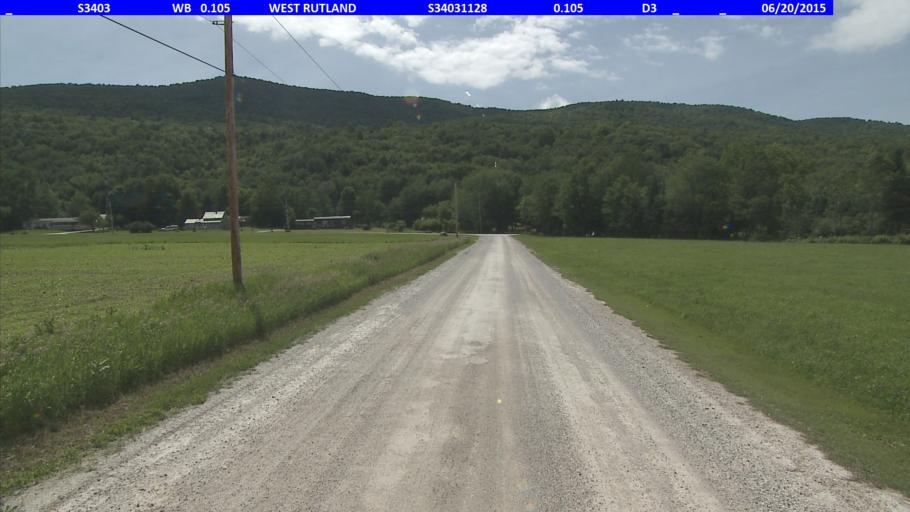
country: US
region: Vermont
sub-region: Rutland County
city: West Rutland
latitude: 43.6312
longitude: -73.0660
